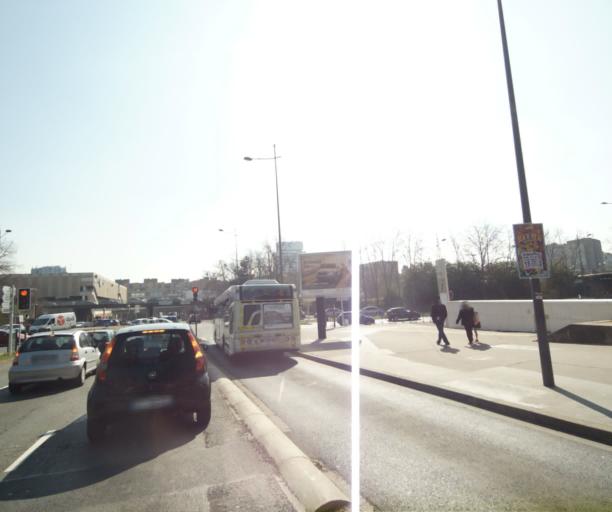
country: FR
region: Ile-de-France
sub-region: Departement du Val-d'Oise
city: Cergy-Pontoise
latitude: 49.0392
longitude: 2.0765
